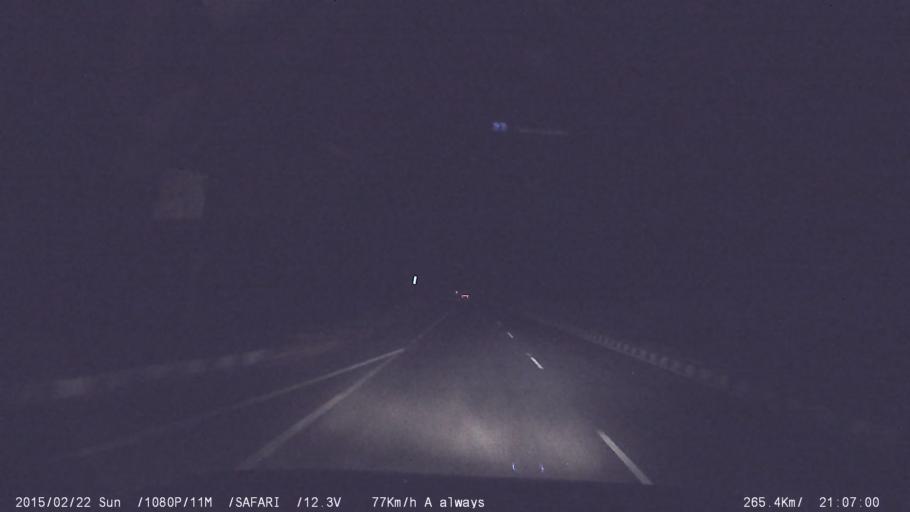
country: IN
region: Tamil Nadu
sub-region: Karur
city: Pallappatti
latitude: 10.7168
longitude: 77.9290
